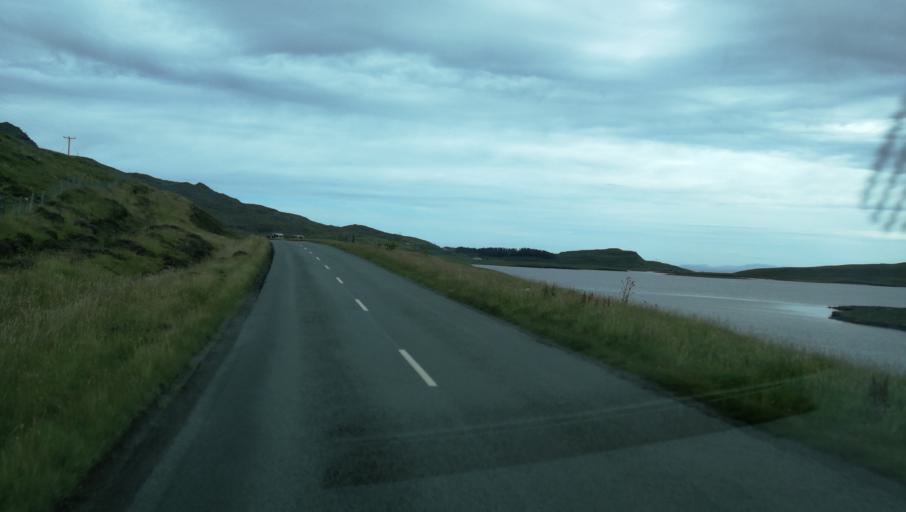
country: GB
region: Scotland
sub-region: Highland
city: Portree
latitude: 57.4838
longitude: -6.1759
